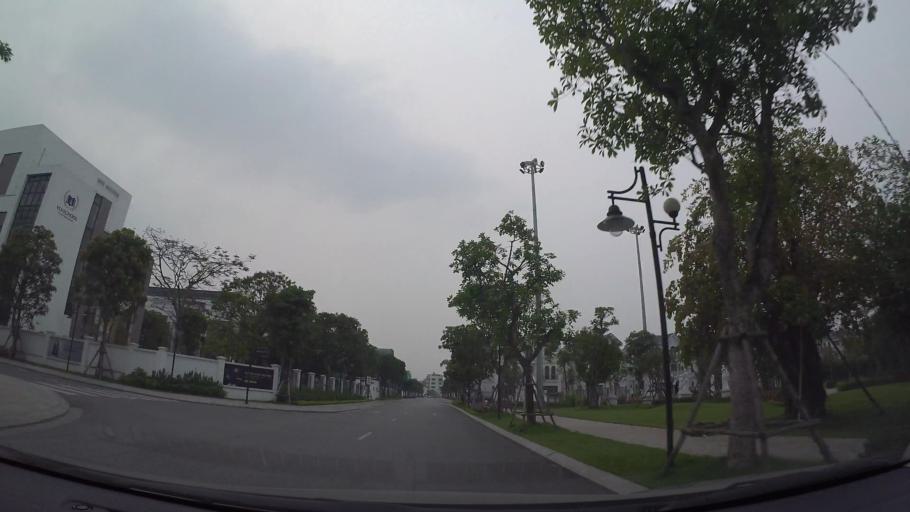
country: VN
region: Ha Noi
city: Trau Quy
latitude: 21.0479
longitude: 105.9048
